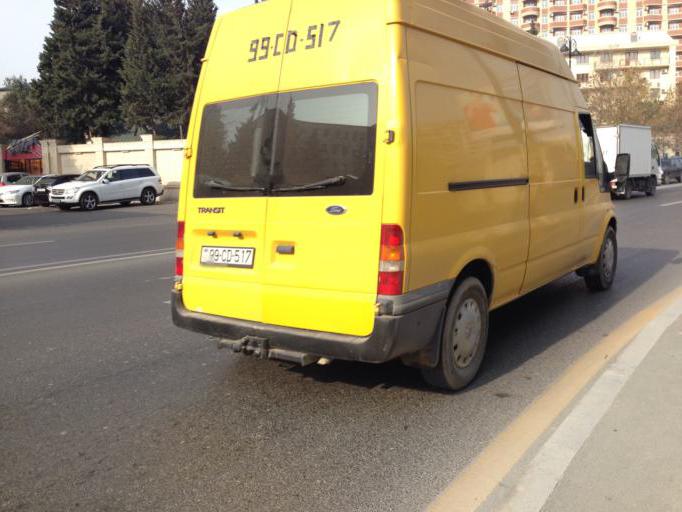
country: AZ
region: Baki
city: Baku
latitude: 40.3958
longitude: 49.8604
